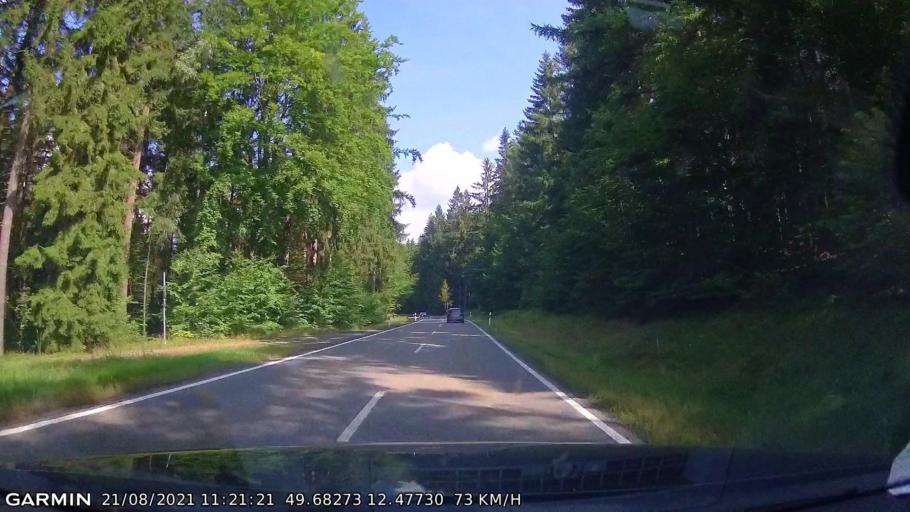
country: DE
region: Bavaria
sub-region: Upper Palatinate
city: Waidhaus
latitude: 49.6827
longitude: 12.4773
